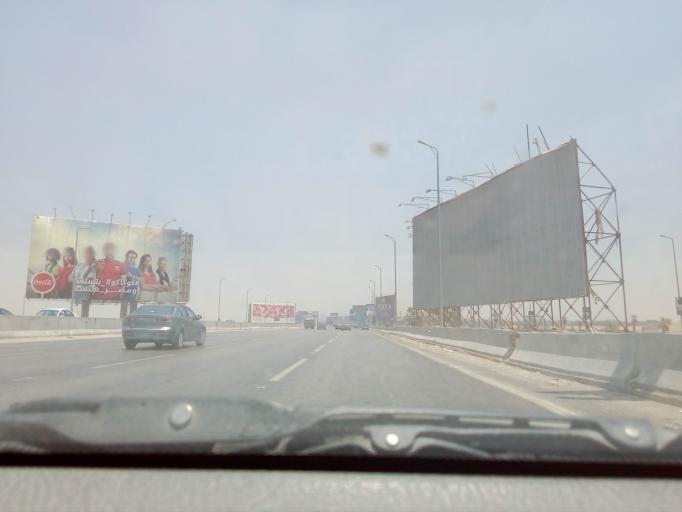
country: EG
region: Muhafazat al Qahirah
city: Cairo
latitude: 29.9892
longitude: 31.3733
